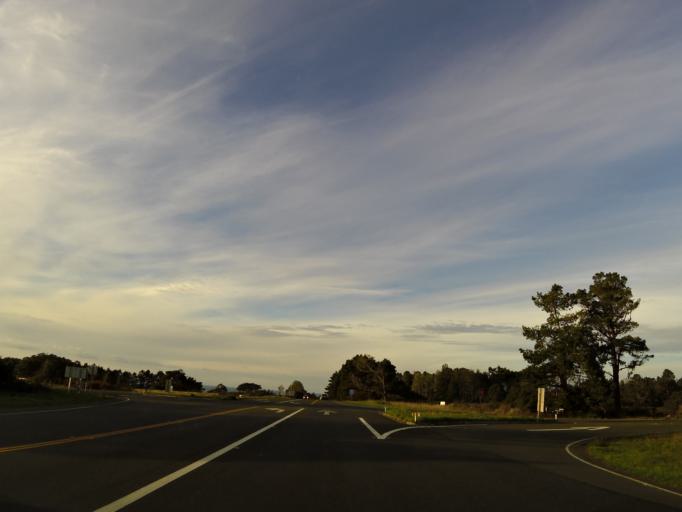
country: US
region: California
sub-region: Mendocino County
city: Fort Bragg
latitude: 39.3646
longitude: -123.8093
